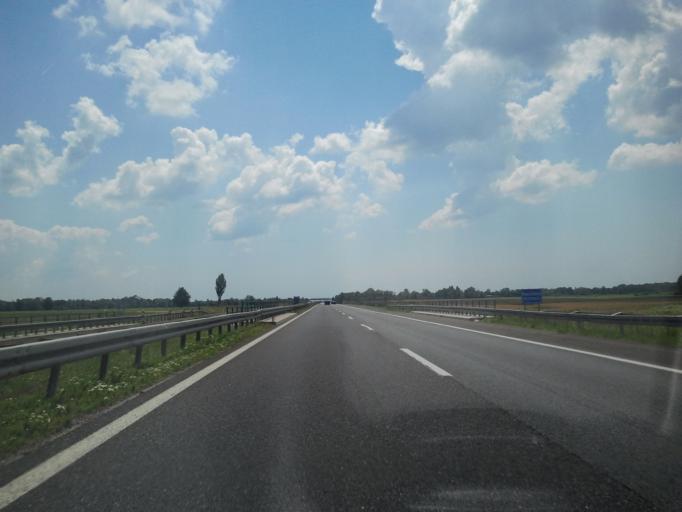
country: HR
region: Zagrebacka
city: Lupoglav
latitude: 45.7259
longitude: 16.3414
